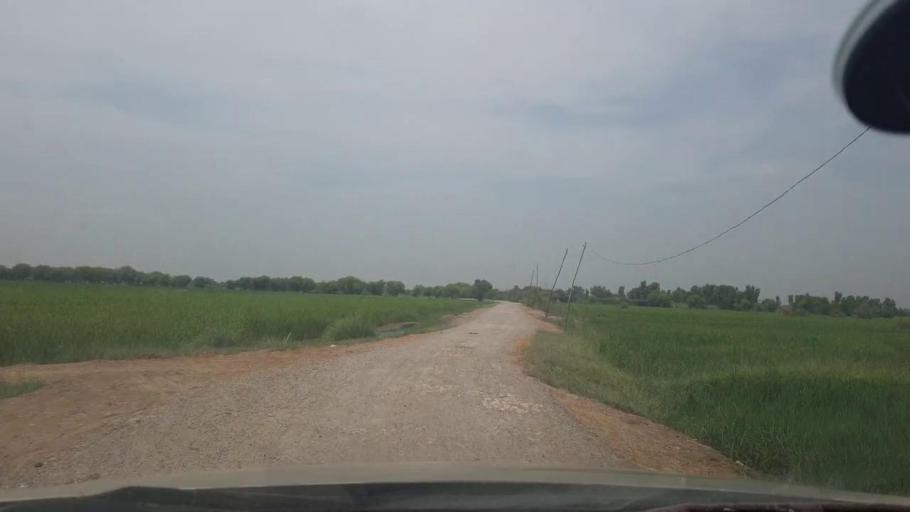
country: PK
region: Sindh
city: Jacobabad
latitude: 28.2415
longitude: 68.4332
